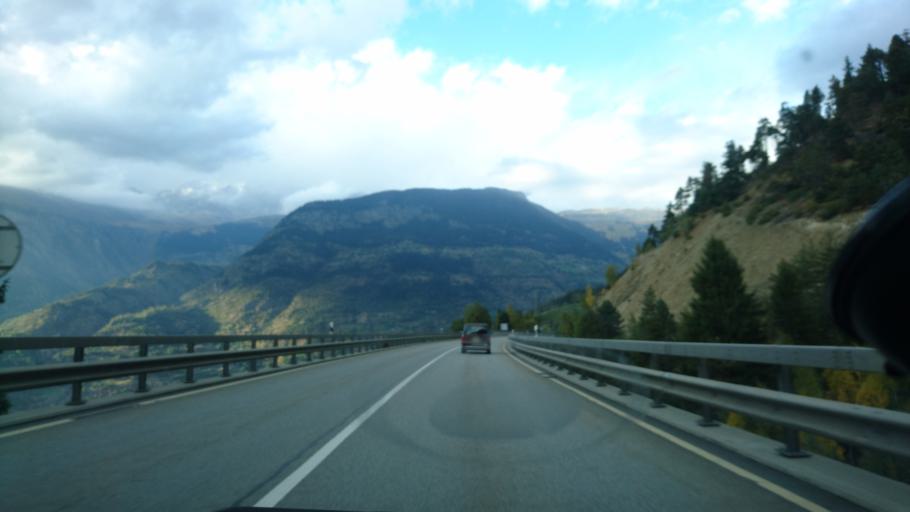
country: CH
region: Valais
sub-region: Brig District
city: Naters
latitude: 46.3199
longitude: 8.0339
